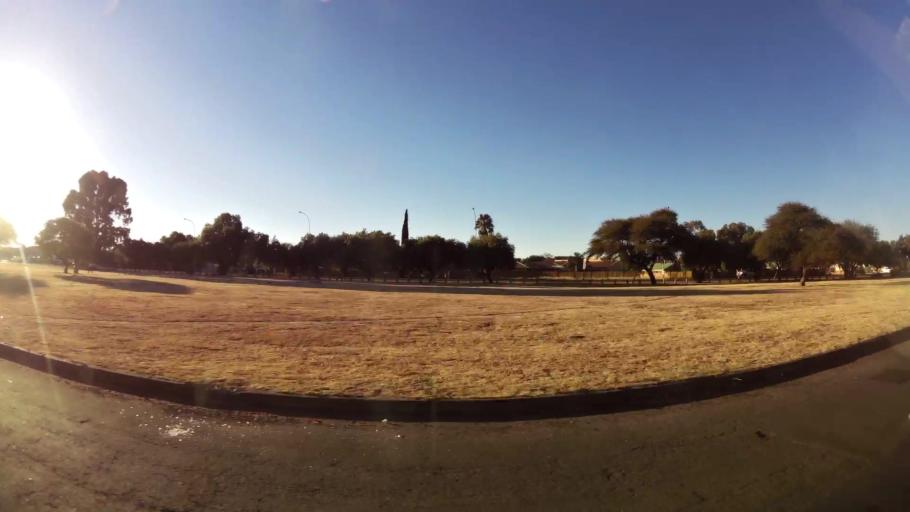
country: ZA
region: Northern Cape
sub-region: Frances Baard District Municipality
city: Kimberley
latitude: -28.7624
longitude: 24.7572
